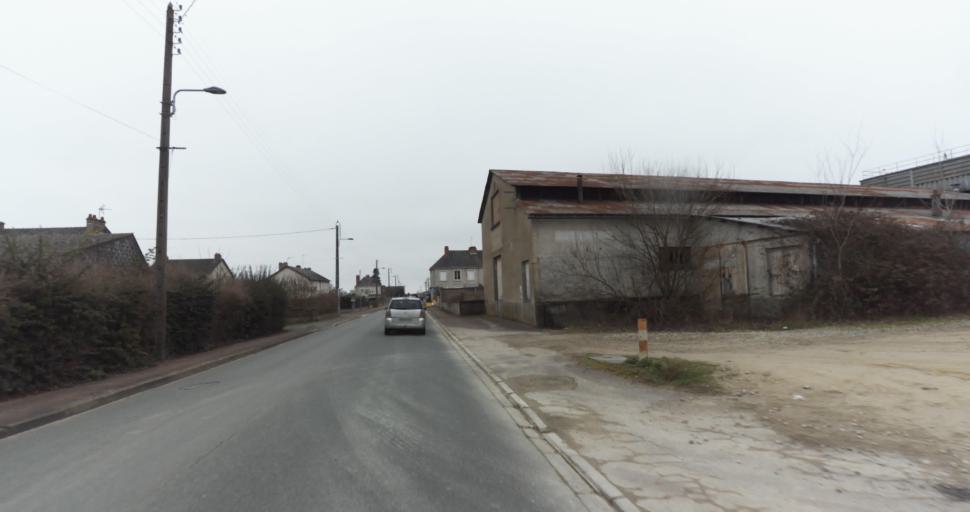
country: FR
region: Pays de la Loire
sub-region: Departement de Maine-et-Loire
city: Montreuil-Bellay
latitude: 47.1259
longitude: -0.1472
